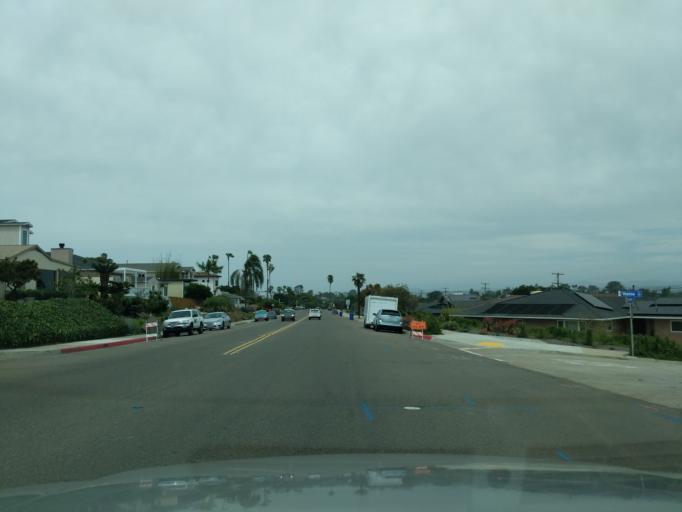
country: US
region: California
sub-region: San Diego County
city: Coronado
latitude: 32.7261
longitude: -117.2445
